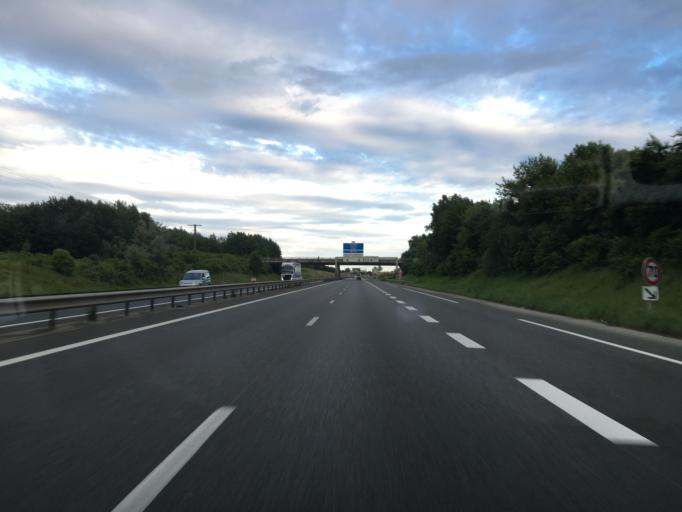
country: FR
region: Ile-de-France
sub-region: Departement de Seine-et-Marne
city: Moissy-Cramayel
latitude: 48.6480
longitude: 2.6214
